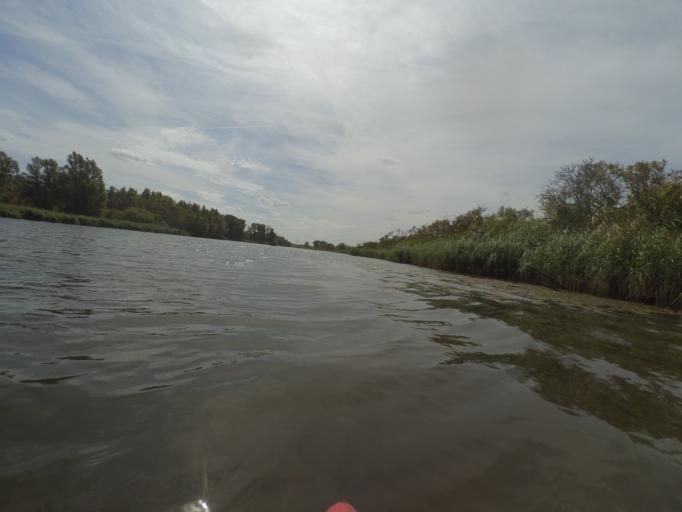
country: NL
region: North Brabant
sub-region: Gemeente Geertruidenberg
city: Geertruidenberg
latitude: 51.7422
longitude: 4.8490
